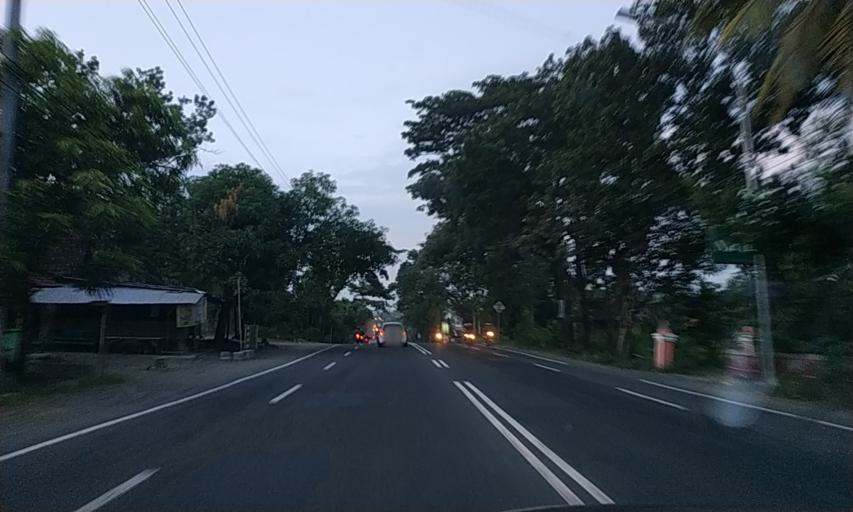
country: ID
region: Daerah Istimewa Yogyakarta
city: Srandakan
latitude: -7.8671
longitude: 110.2101
